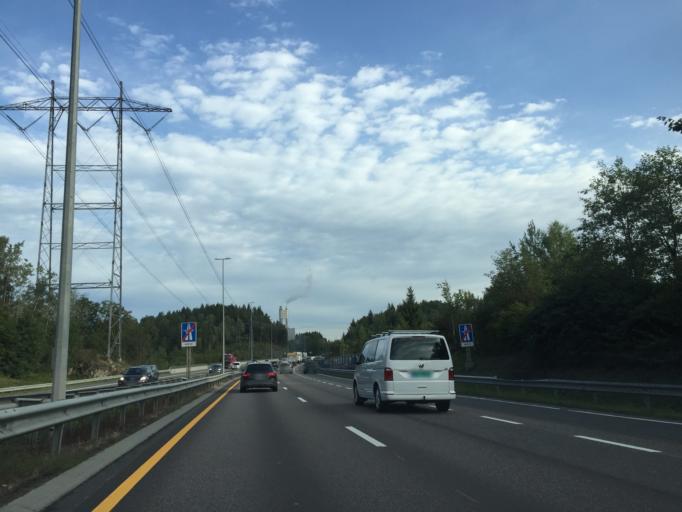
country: NO
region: Akershus
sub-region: Oppegard
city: Kolbotn
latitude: 59.8328
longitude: 10.8407
